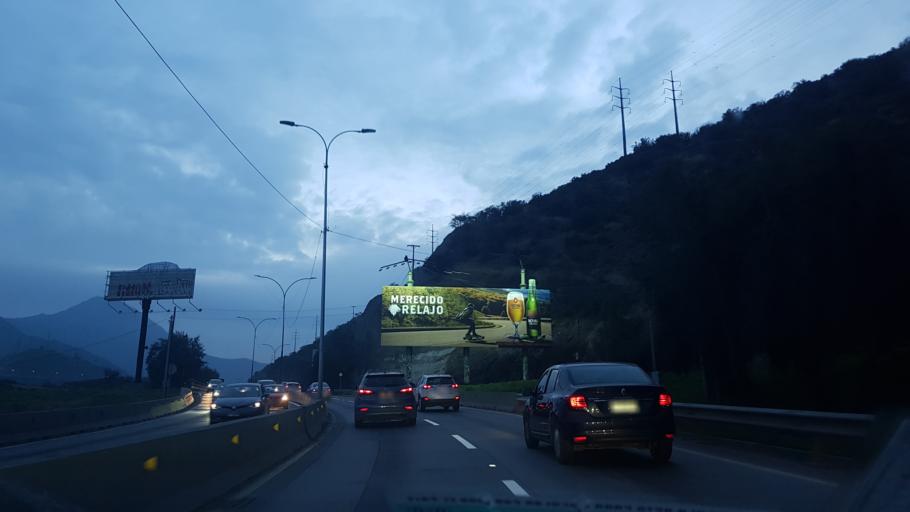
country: CL
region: Santiago Metropolitan
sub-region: Provincia de Santiago
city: Santiago
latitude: -33.3963
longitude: -70.6113
